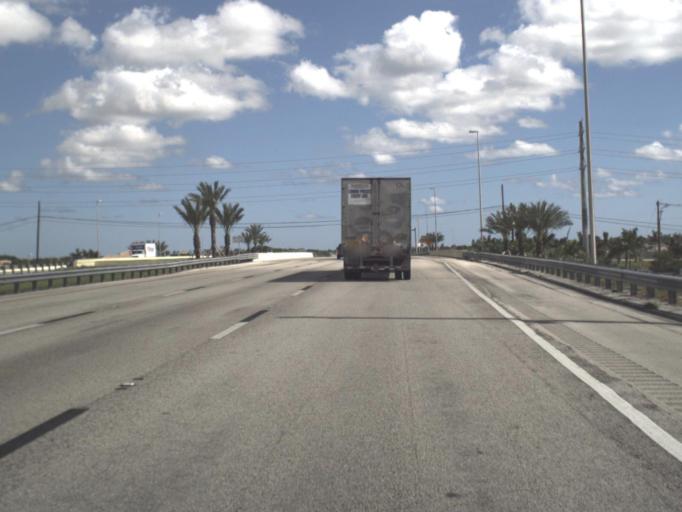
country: US
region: Florida
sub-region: Broward County
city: Parkland
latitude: 26.2999
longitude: -80.2038
